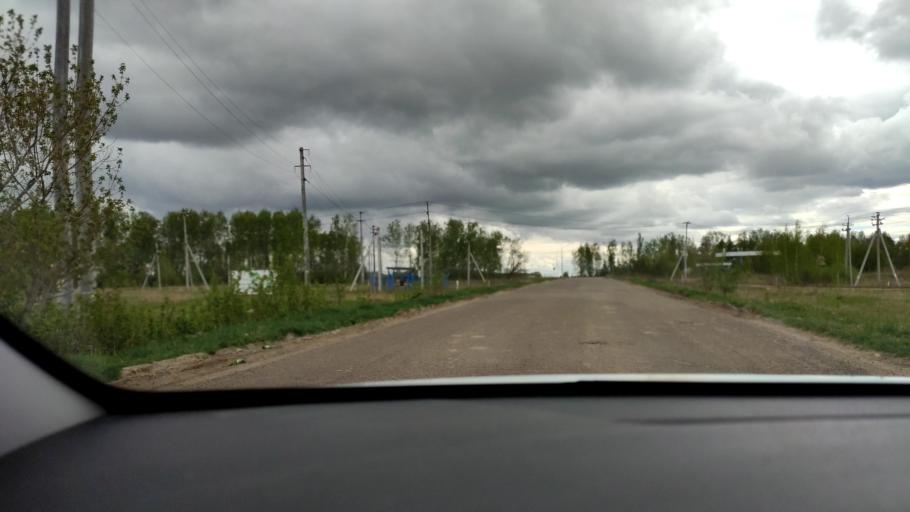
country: RU
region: Tatarstan
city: Vysokaya Gora
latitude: 55.8030
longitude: 49.3131
